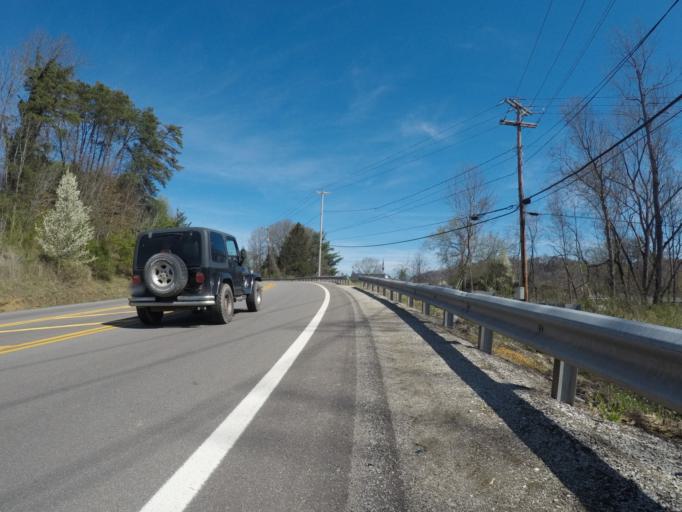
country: US
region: West Virginia
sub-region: Cabell County
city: Pea Ridge
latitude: 38.3978
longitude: -82.3205
